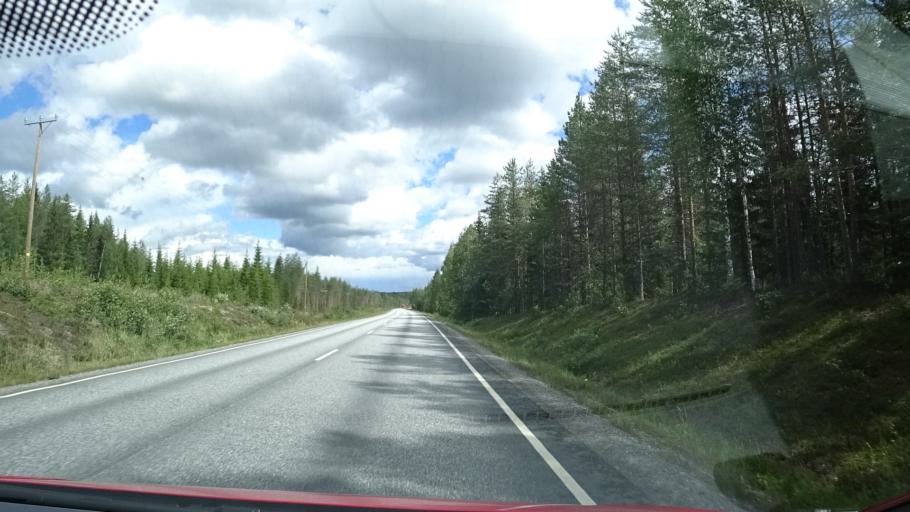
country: FI
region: Northern Savo
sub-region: Koillis-Savo
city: Rautavaara
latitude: 63.3491
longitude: 28.4902
